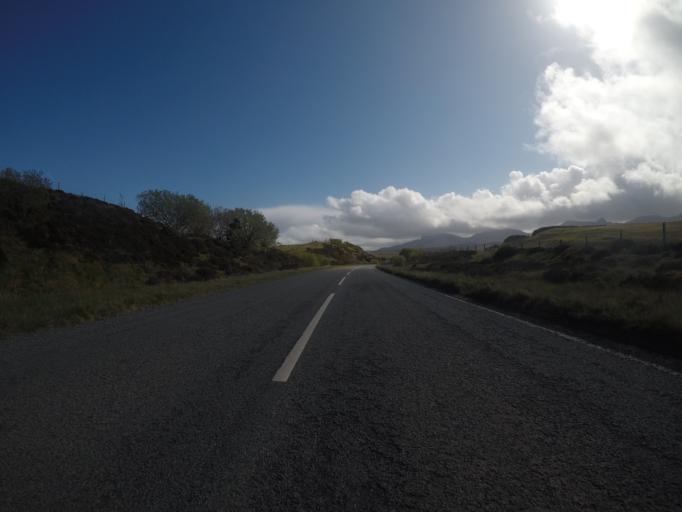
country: GB
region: Scotland
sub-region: Highland
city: Portree
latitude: 57.5873
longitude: -6.1572
